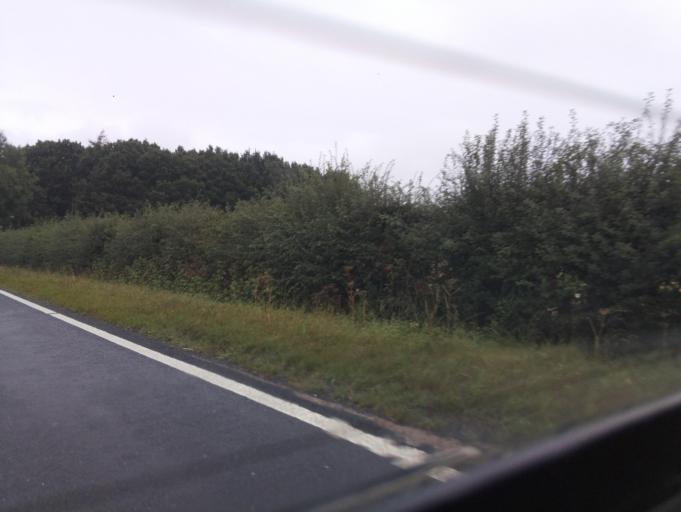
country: GB
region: England
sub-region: North Yorkshire
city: Pannal
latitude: 53.9216
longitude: -1.5304
